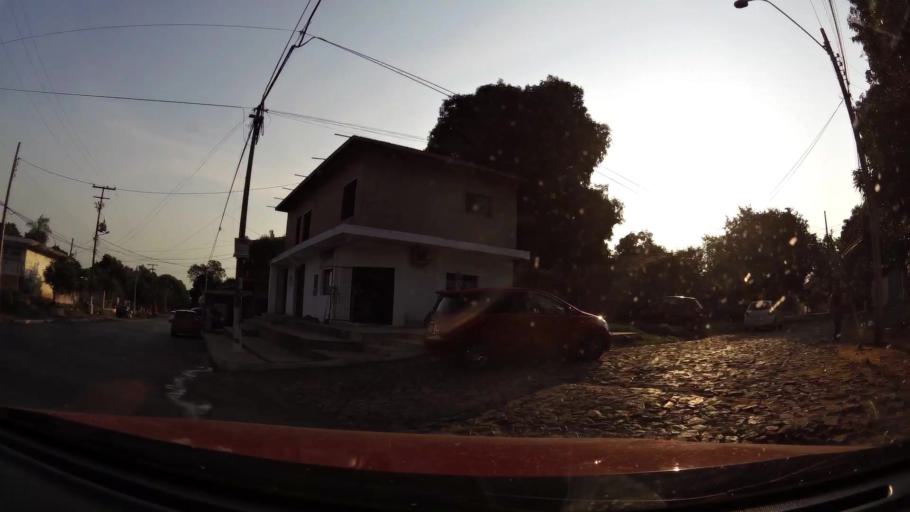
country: PY
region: Central
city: Villa Elisa
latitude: -25.3580
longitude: -57.5993
